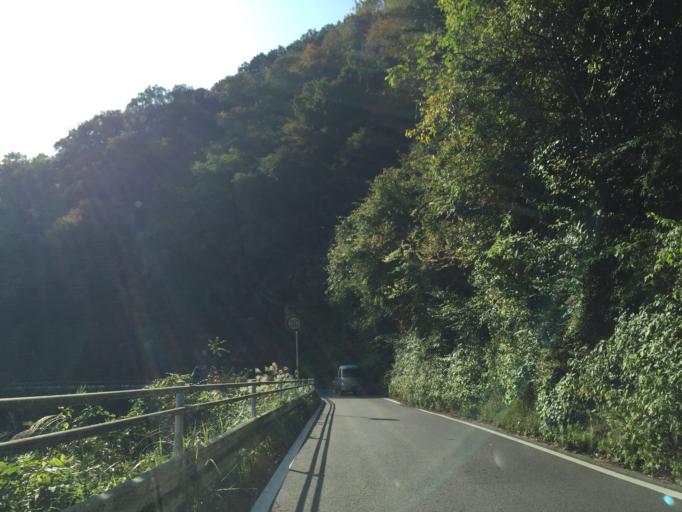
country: JP
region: Gifu
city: Minokamo
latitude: 35.5460
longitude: 137.1187
